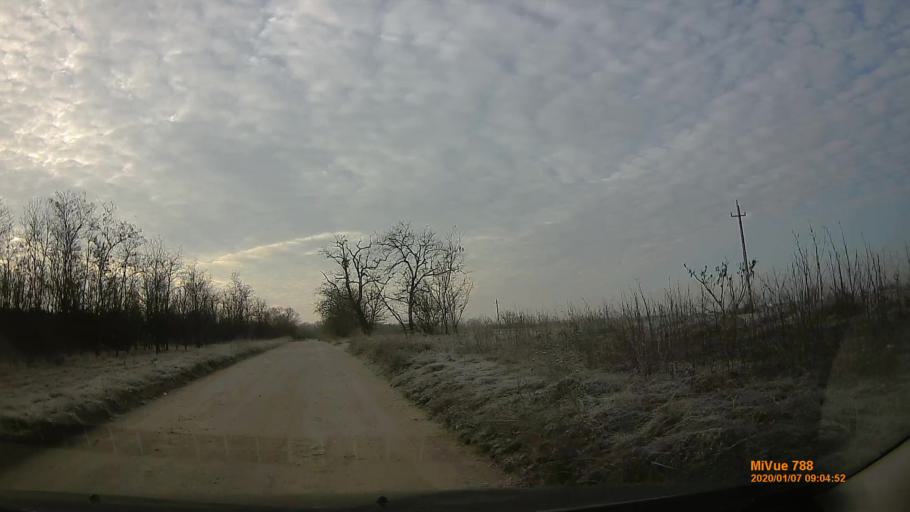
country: HU
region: Gyor-Moson-Sopron
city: Rajka
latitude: 47.9832
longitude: 17.1894
